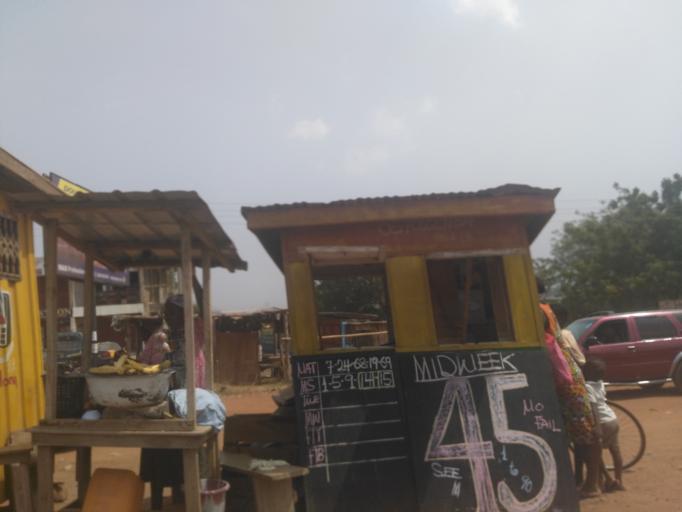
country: GH
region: Greater Accra
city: Tema
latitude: 5.6949
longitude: -0.0136
